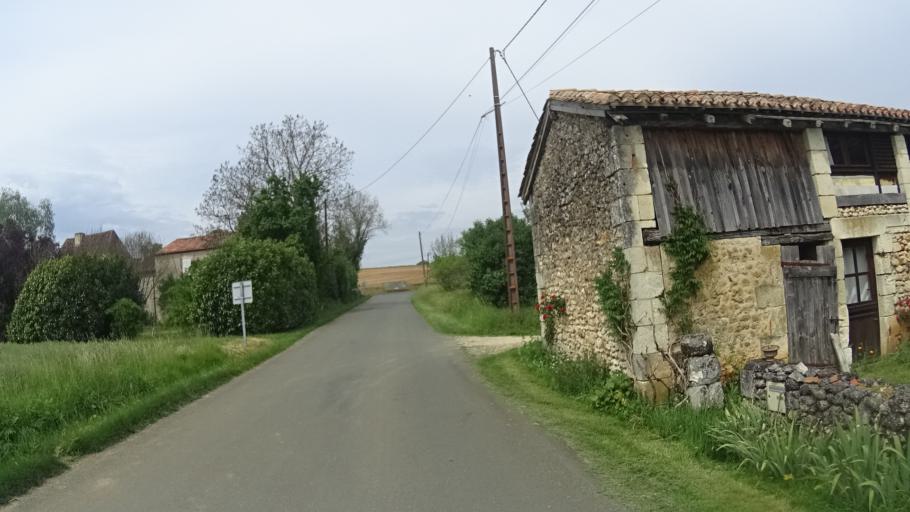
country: FR
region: Aquitaine
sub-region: Departement de la Dordogne
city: Lembras
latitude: 44.9951
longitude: 0.5277
